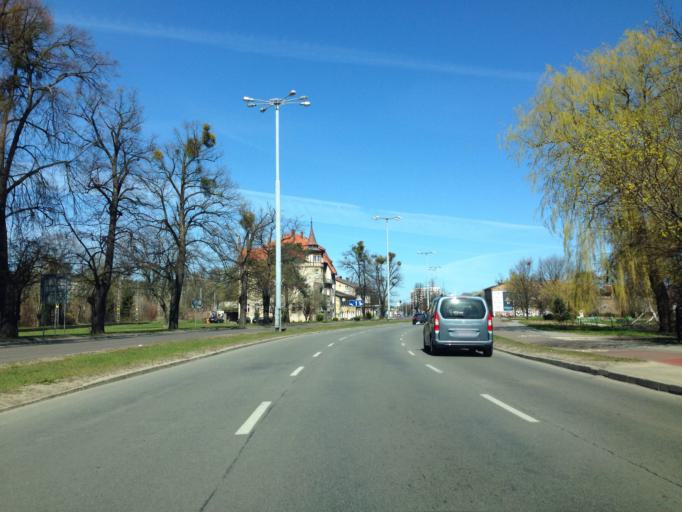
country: PL
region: Pomeranian Voivodeship
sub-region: Sopot
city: Sopot
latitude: 54.4119
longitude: 18.5664
